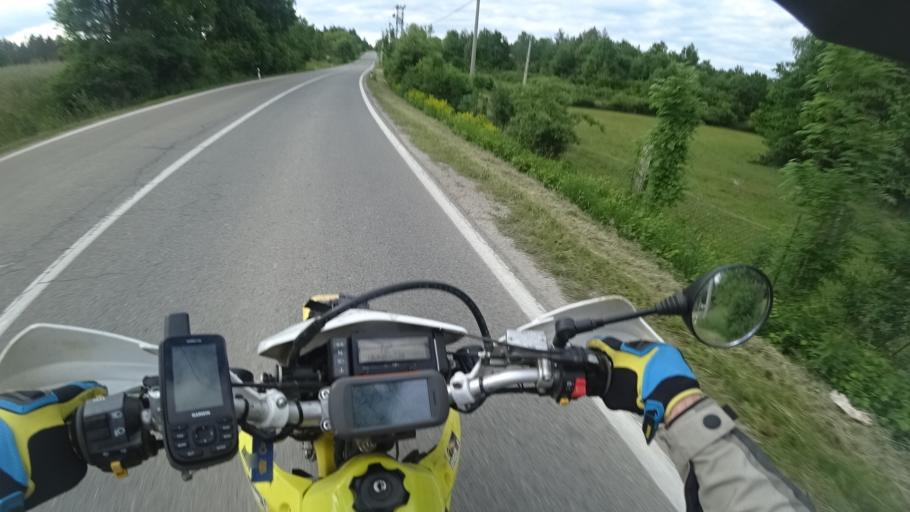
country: HR
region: Licko-Senjska
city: Gospic
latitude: 44.5180
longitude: 15.4164
